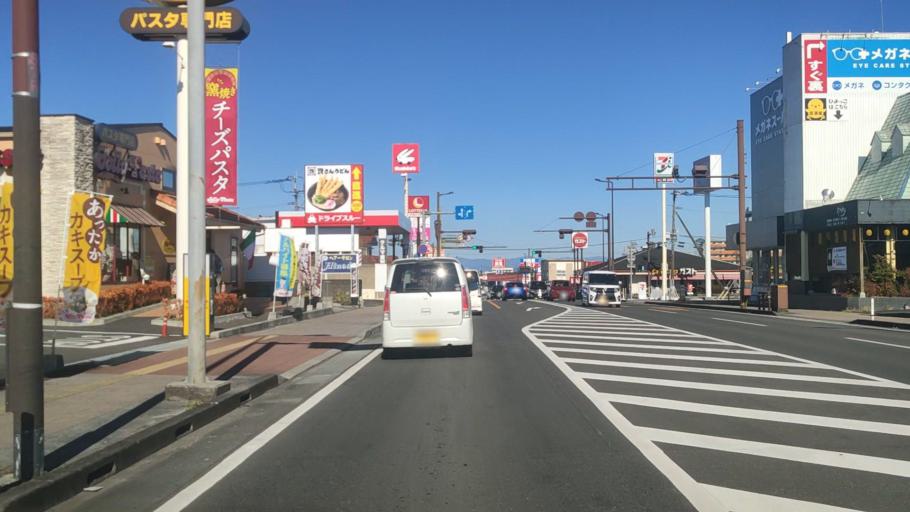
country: JP
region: Miyazaki
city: Miyakonojo
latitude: 31.7346
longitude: 131.0688
